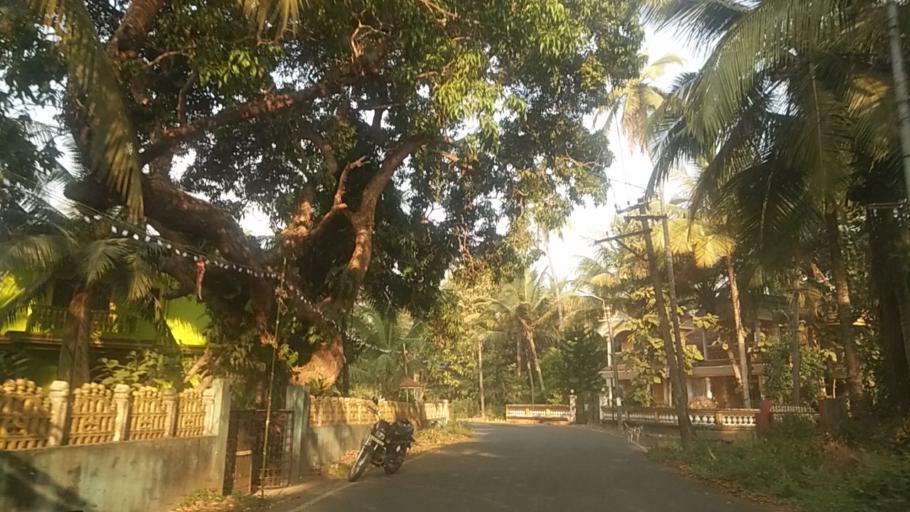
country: IN
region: Goa
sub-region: South Goa
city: Chinchinim
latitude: 15.2325
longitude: 73.9919
